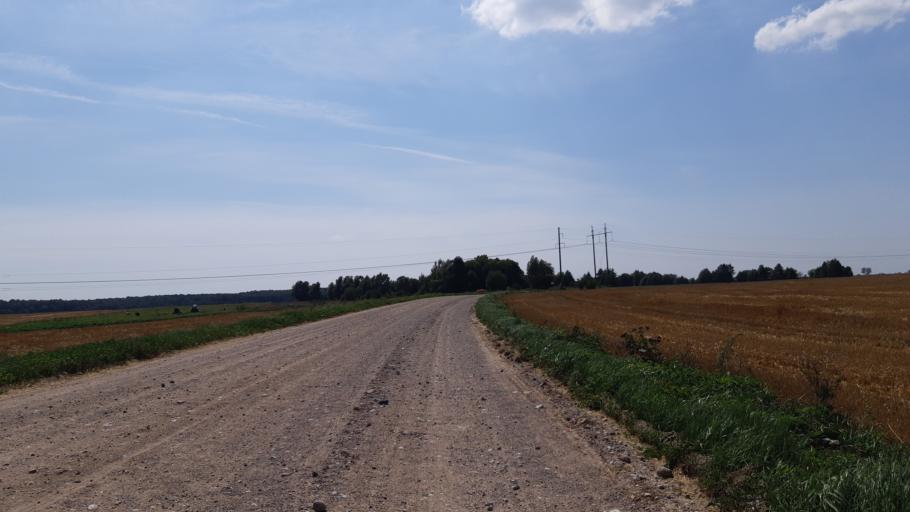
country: LT
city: Virbalis
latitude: 54.6209
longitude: 22.8072
